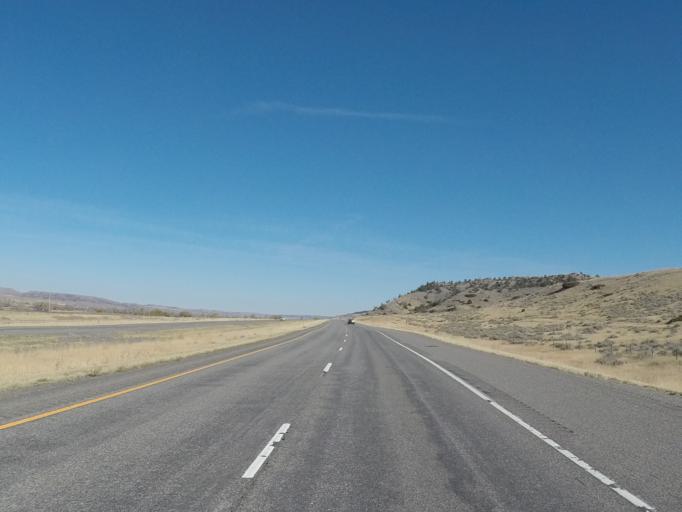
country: US
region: Montana
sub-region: Sweet Grass County
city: Big Timber
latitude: 45.7667
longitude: -110.0883
